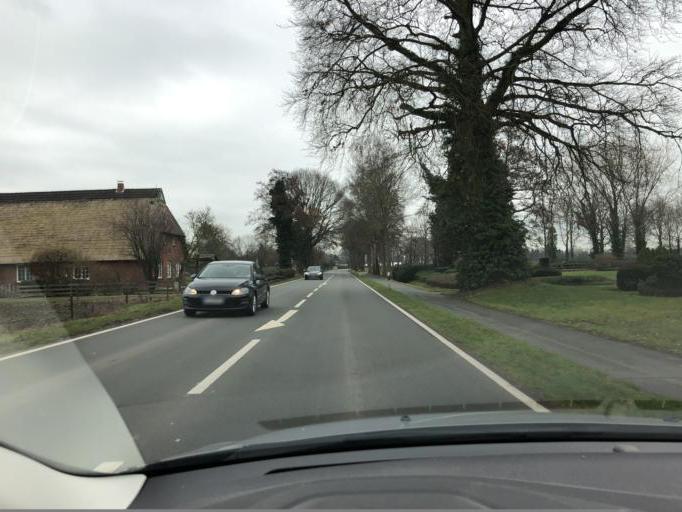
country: DE
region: Lower Saxony
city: Ganderkesee
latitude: 53.0960
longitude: 8.5721
